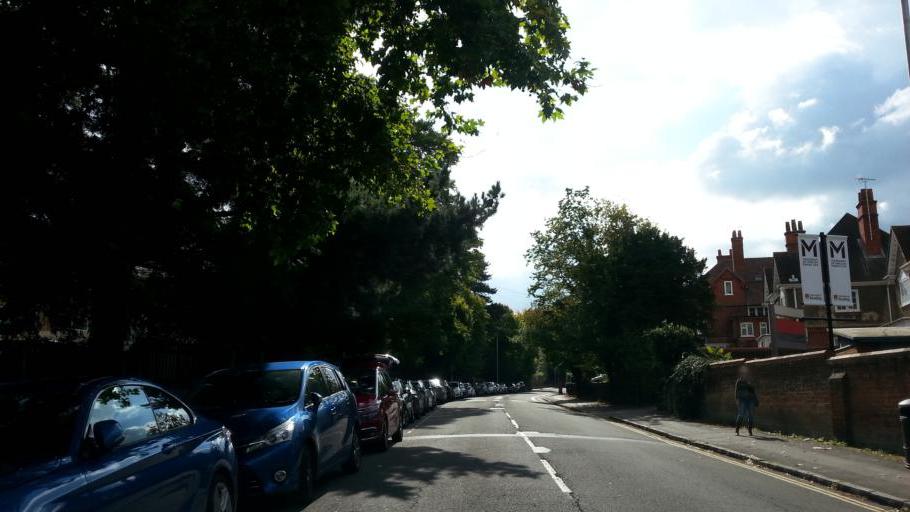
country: GB
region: England
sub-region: Reading
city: Reading
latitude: 51.4490
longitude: -0.9592
